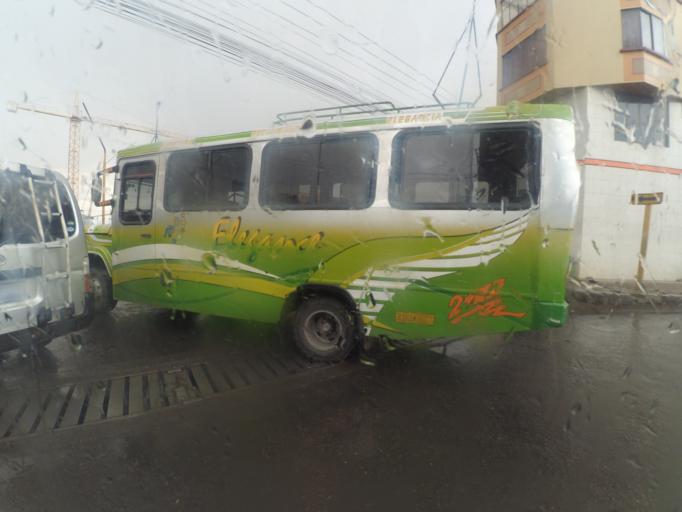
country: BO
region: La Paz
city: La Paz
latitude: -16.5225
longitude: -68.1687
